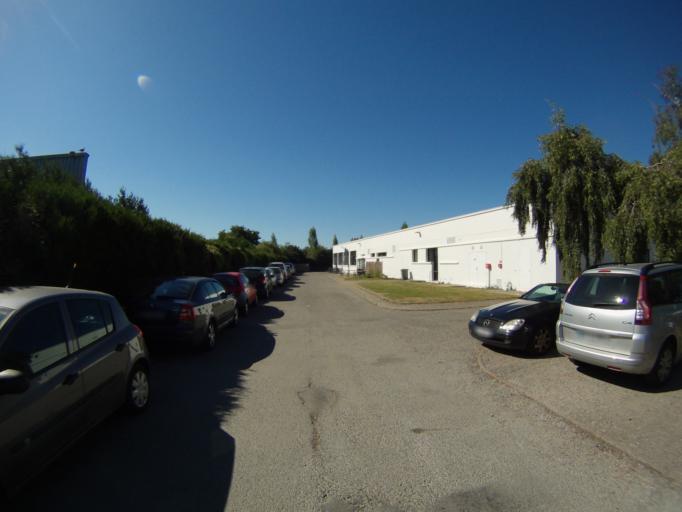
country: FR
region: Brittany
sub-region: Departement d'Ille-et-Vilaine
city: Vezin-le-Coquet
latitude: 48.1020
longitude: -1.7254
